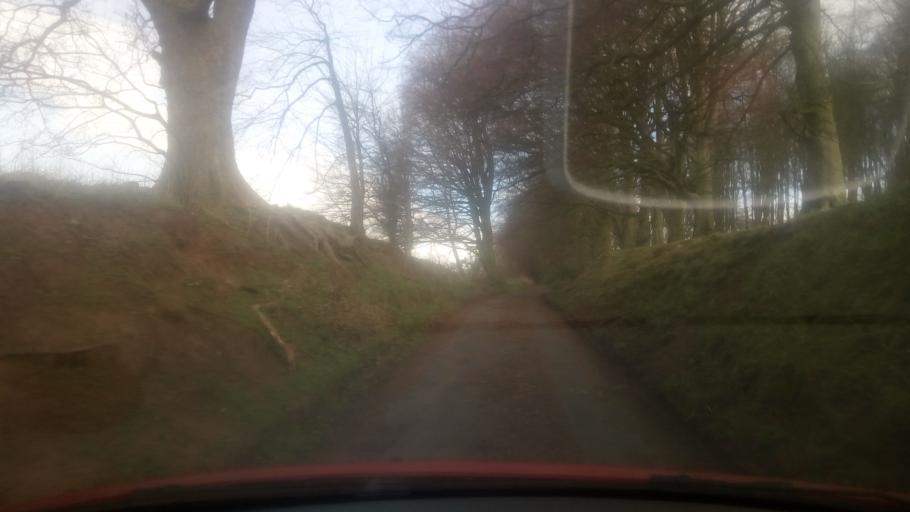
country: GB
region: Scotland
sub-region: The Scottish Borders
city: Jedburgh
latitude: 55.4958
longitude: -2.5361
